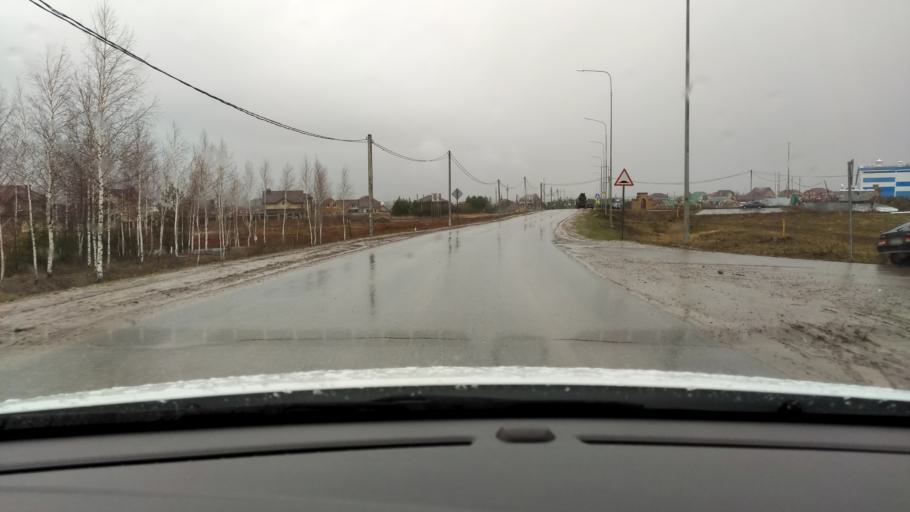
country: RU
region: Tatarstan
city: Vysokaya Gora
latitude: 55.9010
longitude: 49.3251
